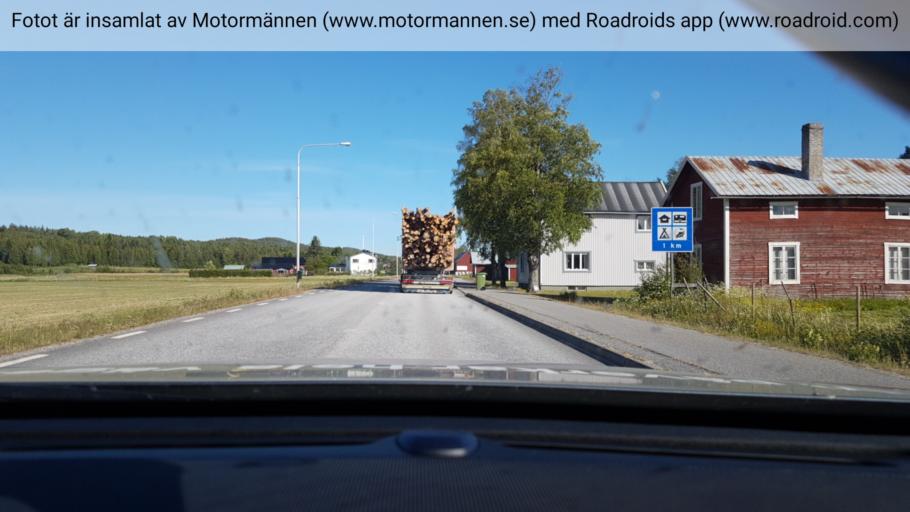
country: SE
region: Vaesterbotten
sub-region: Bjurholms Kommun
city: Bjurholm
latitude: 64.2572
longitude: 19.2927
